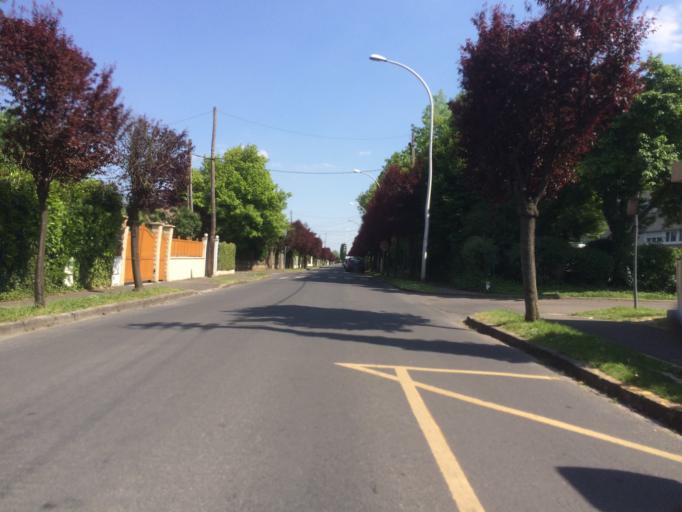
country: FR
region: Ile-de-France
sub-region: Departement de l'Essonne
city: Morangis
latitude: 48.6930
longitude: 2.3459
